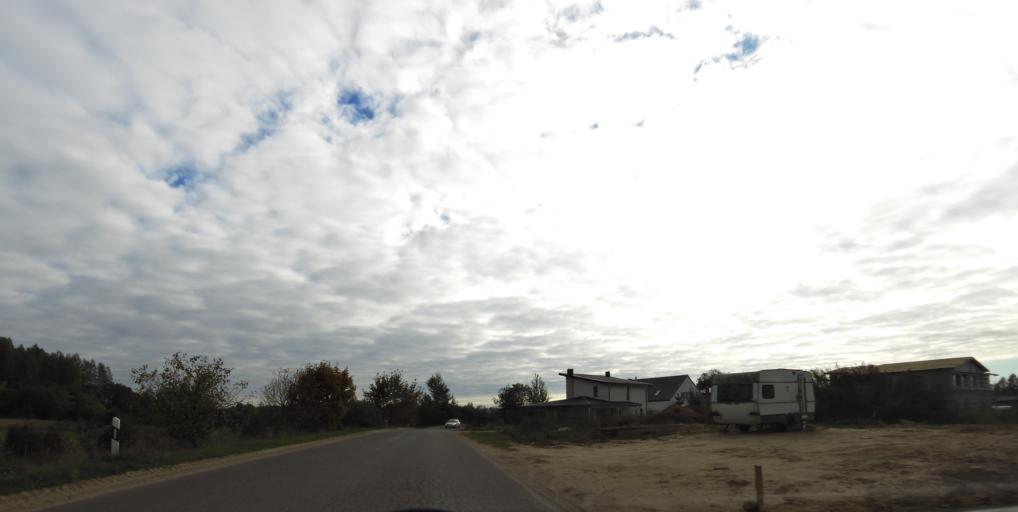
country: LT
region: Vilnius County
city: Pilaite
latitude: 54.7218
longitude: 25.1560
